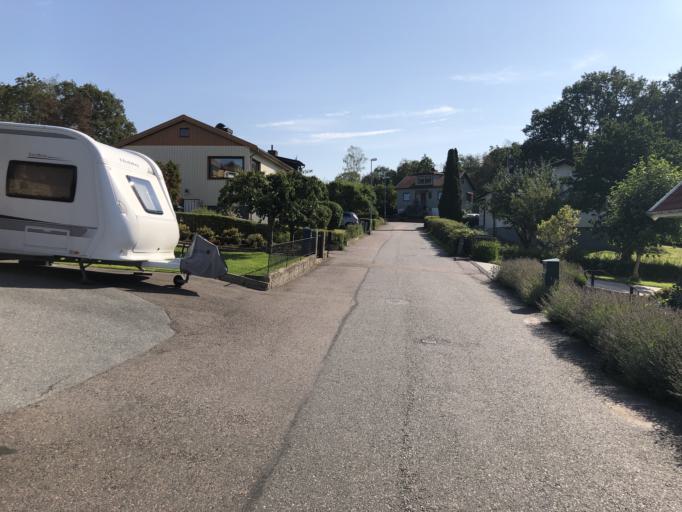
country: SE
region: Vaestra Goetaland
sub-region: Goteborg
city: Goeteborg
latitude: 57.7394
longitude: 11.9634
